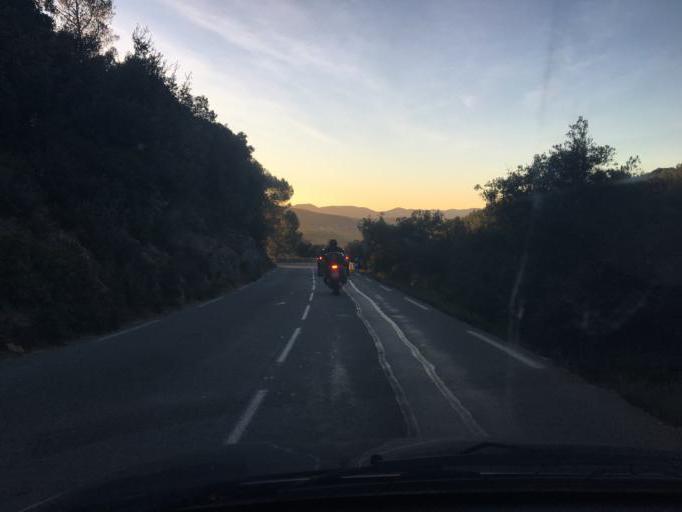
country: FR
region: Provence-Alpes-Cote d'Azur
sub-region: Departement du Var
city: Taradeau
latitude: 43.4586
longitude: 6.4197
